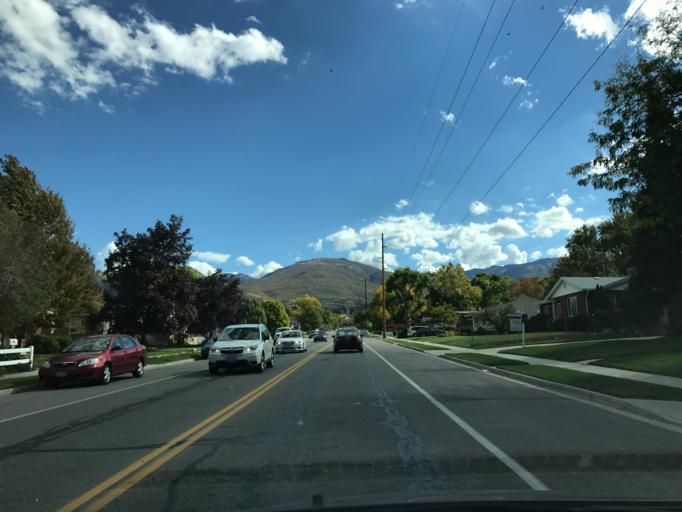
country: US
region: Utah
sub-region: Davis County
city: Woods Cross
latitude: 40.8711
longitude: -111.8848
